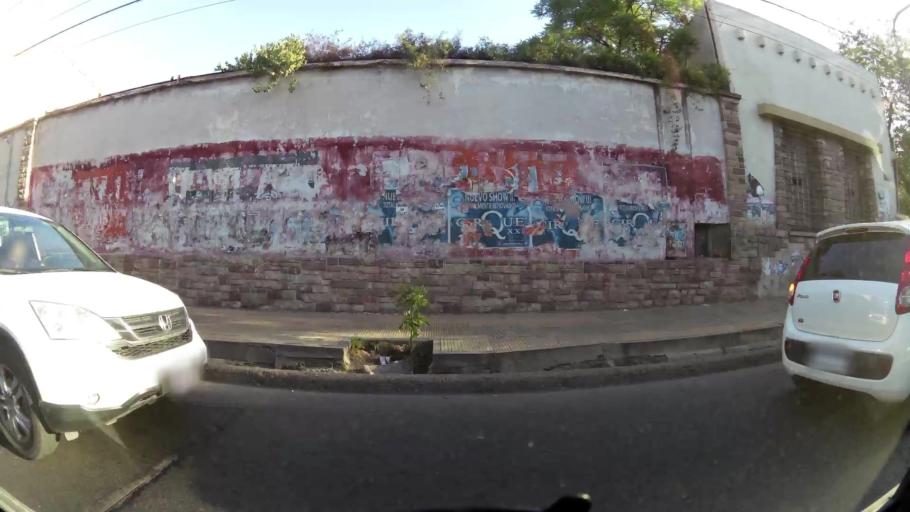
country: AR
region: Mendoza
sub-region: Departamento de Godoy Cruz
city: Godoy Cruz
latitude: -32.9082
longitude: -68.8437
